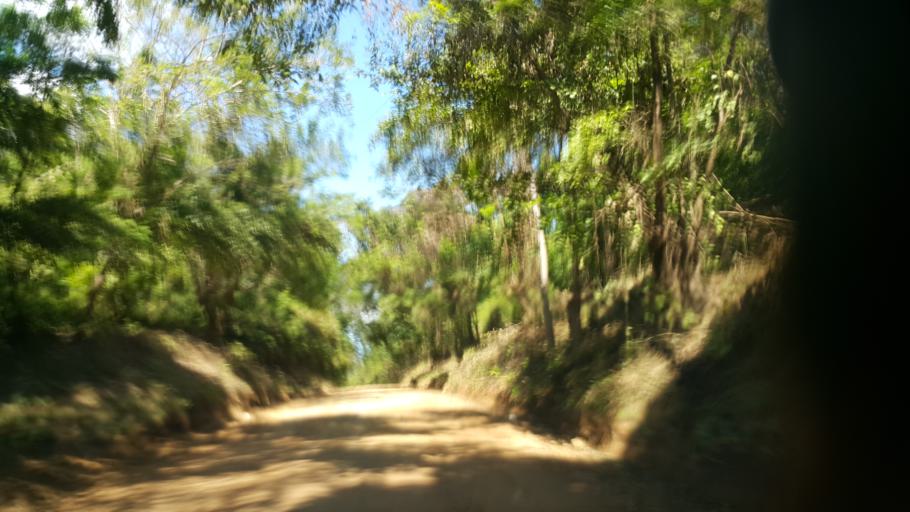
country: NI
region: Rivas
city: San Juan del Sur
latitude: 11.2794
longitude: -85.8887
